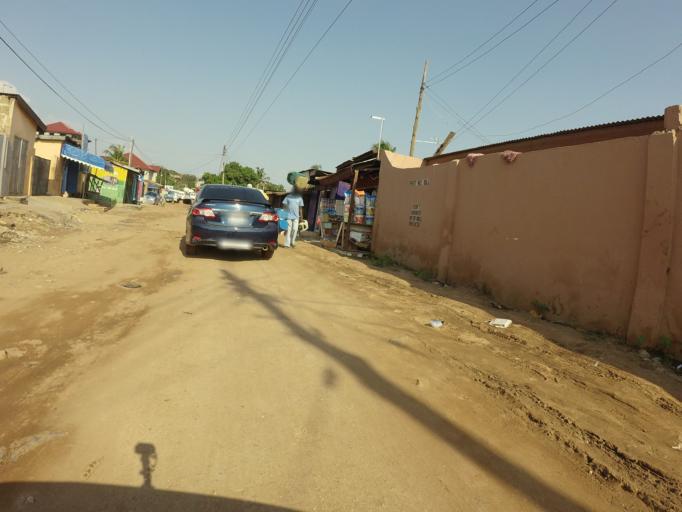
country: GH
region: Greater Accra
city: Dome
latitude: 5.6089
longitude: -0.2446
